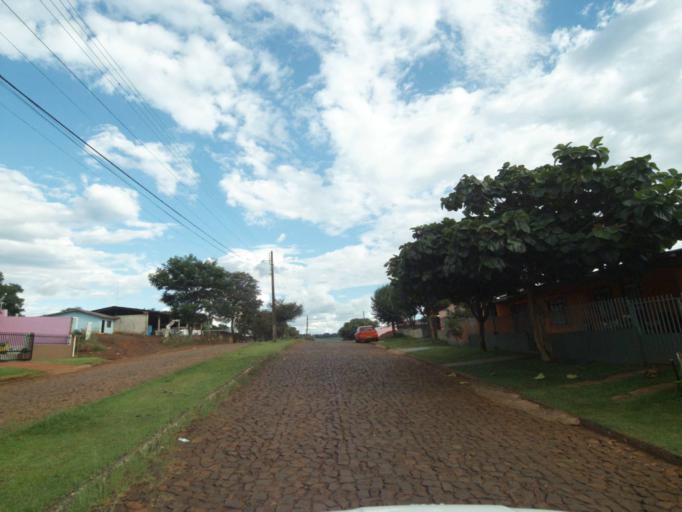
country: BR
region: Parana
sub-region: Laranjeiras Do Sul
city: Laranjeiras do Sul
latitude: -25.4932
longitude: -52.5271
